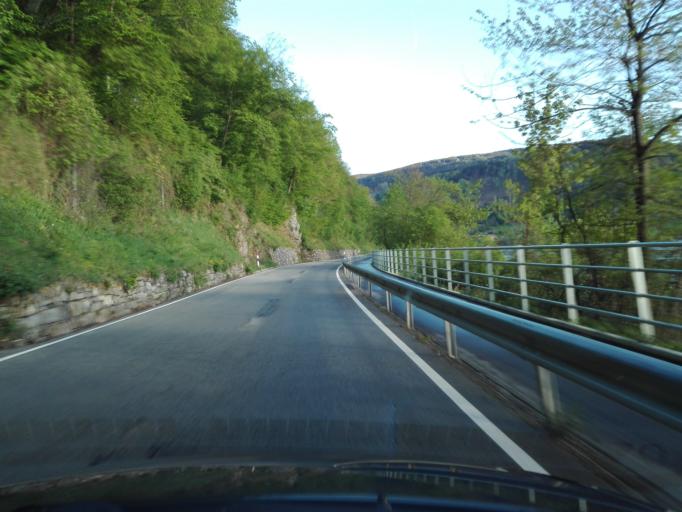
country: DE
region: Bavaria
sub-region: Lower Bavaria
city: Obernzell
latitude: 48.5453
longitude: 13.6582
